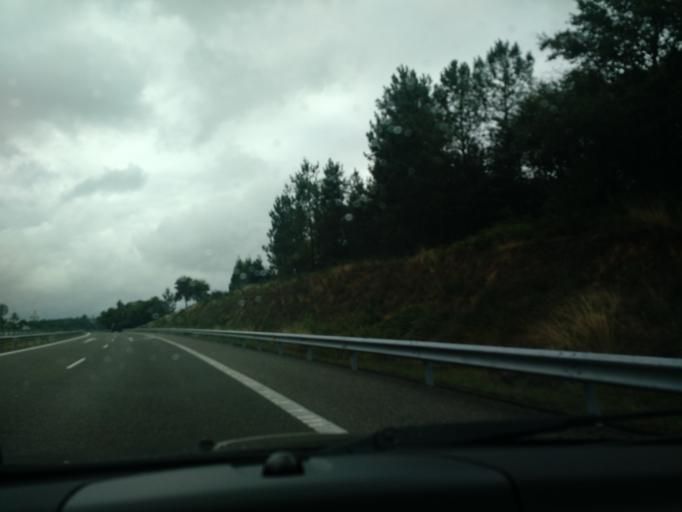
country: ES
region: Galicia
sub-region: Provincia da Coruna
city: Oroso
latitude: 42.9339
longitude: -8.4667
